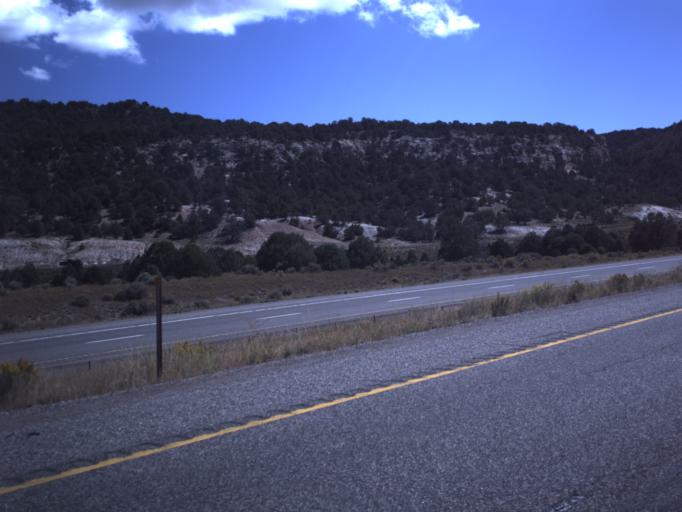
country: US
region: Utah
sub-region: Sevier County
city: Salina
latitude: 38.8757
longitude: -111.5557
